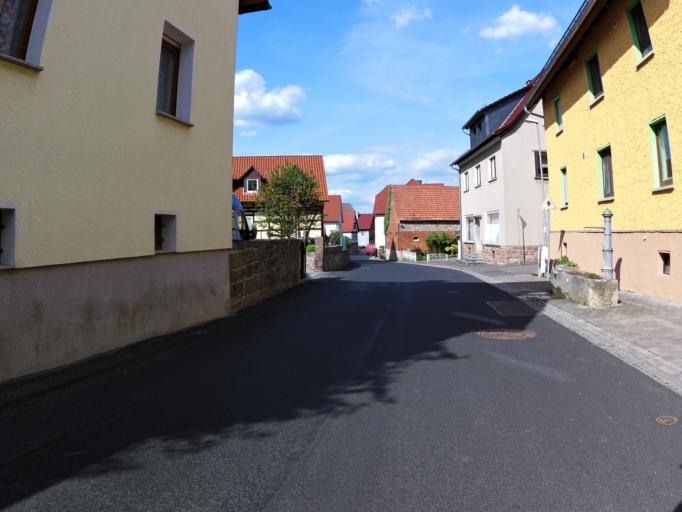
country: DE
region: Thuringia
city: Dermbach
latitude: 50.7146
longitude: 10.1147
